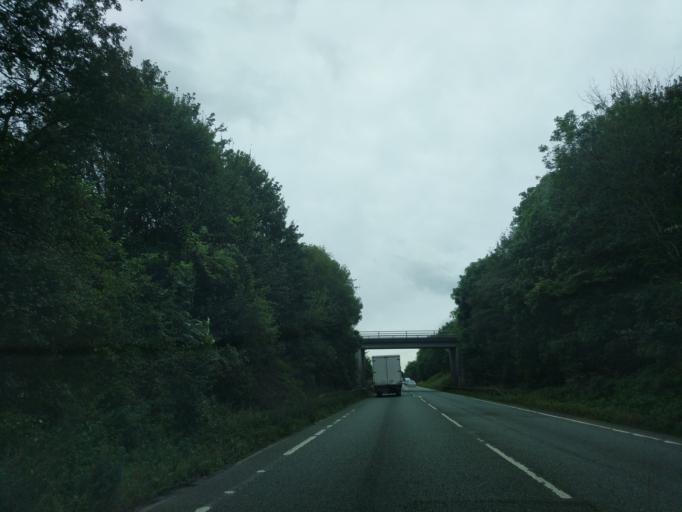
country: GB
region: England
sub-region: Cheshire East
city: Alsager
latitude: 53.0711
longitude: -2.3455
